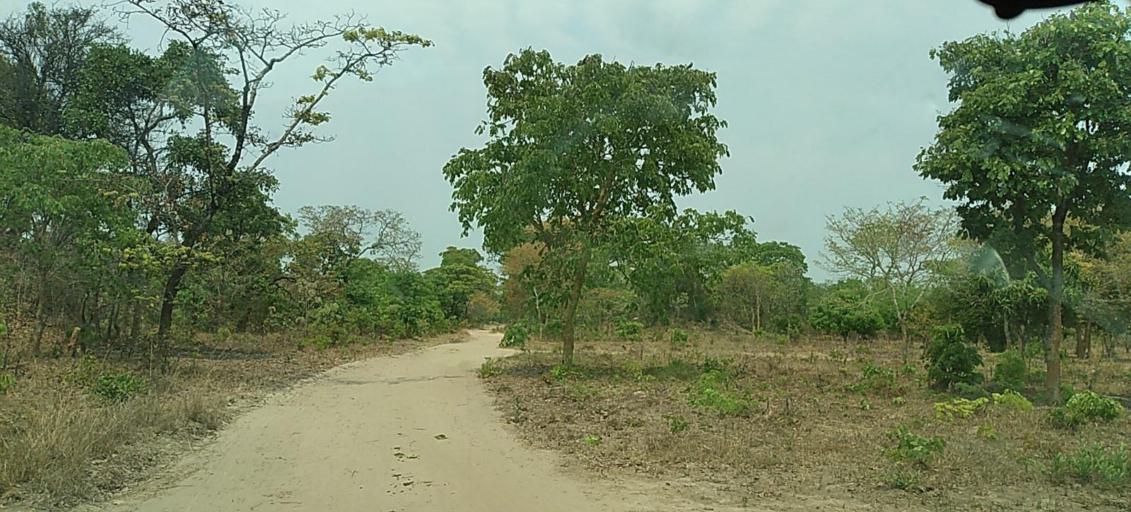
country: ZM
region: North-Western
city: Kabompo
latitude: -13.5555
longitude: 24.4476
